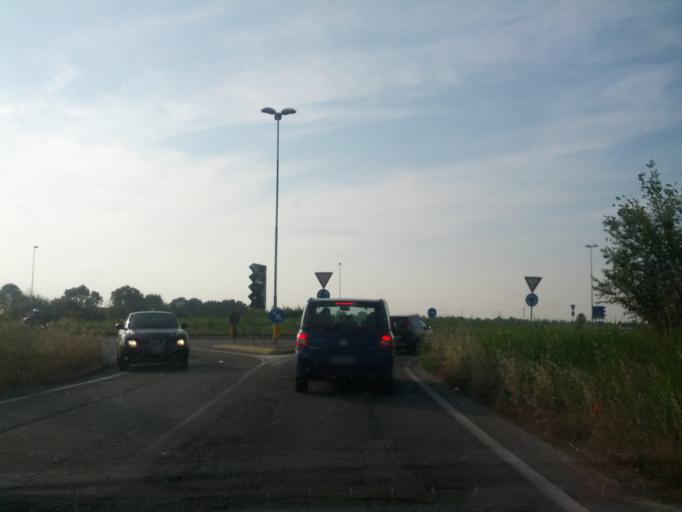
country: IT
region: Emilia-Romagna
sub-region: Provincia di Reggio Emilia
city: Bagnolo in Piano
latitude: 44.7576
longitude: 10.6592
